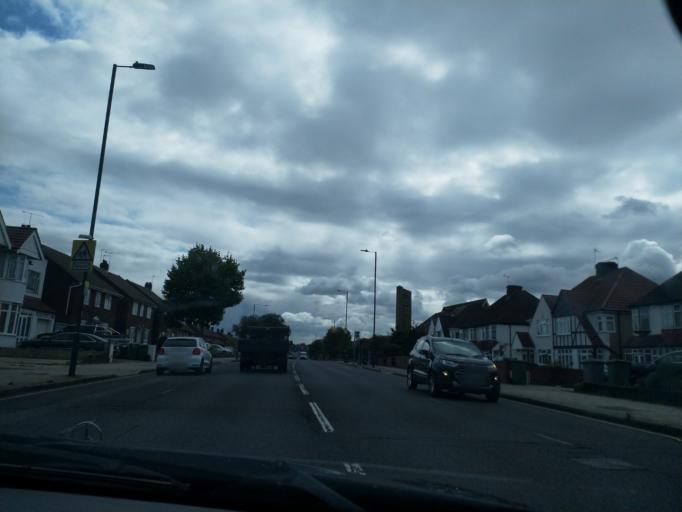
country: GB
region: England
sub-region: Greater London
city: Edgware
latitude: 51.5867
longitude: -0.2949
